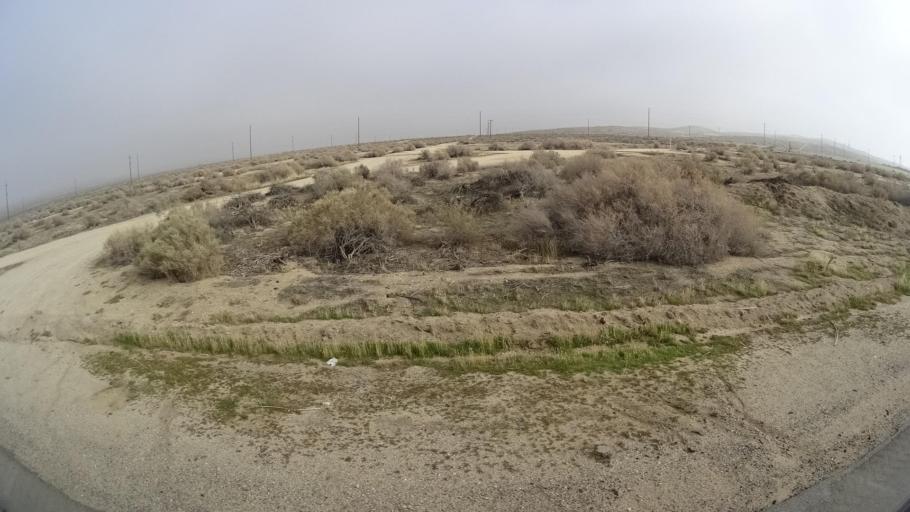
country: US
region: California
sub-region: Kern County
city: Ford City
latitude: 35.1791
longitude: -119.4291
